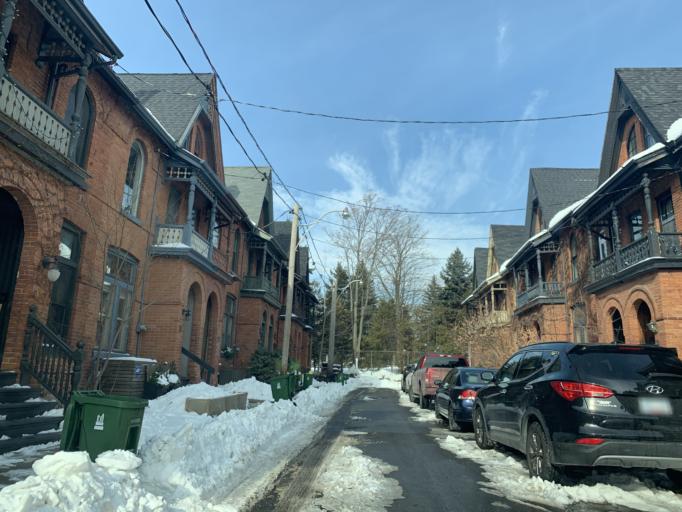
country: CA
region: Ontario
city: Toronto
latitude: 43.6689
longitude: -79.3683
